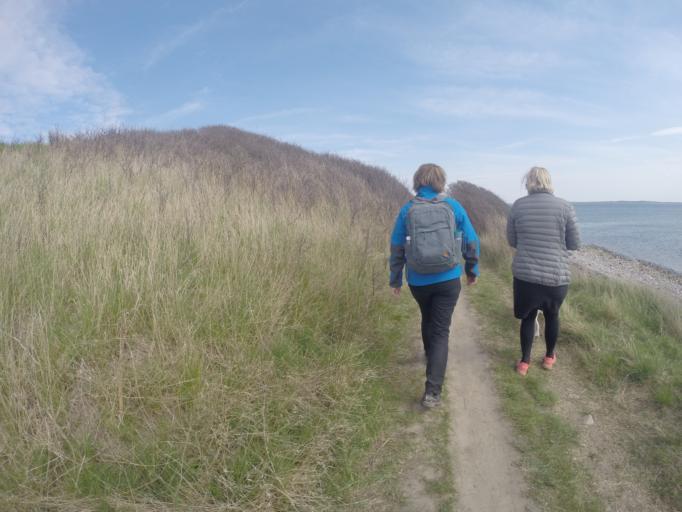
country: DK
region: Zealand
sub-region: Kalundborg Kommune
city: Gorlev
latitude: 55.5108
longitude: 11.1023
